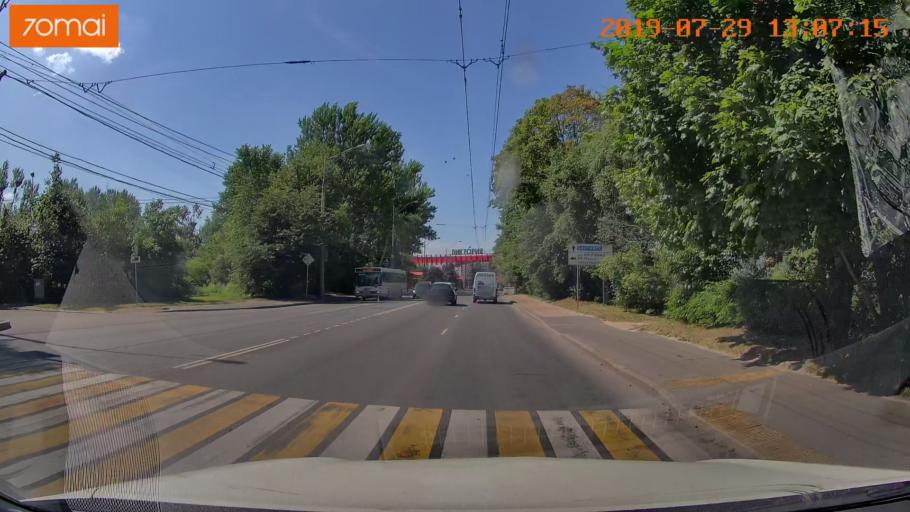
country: RU
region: Kaliningrad
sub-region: Gorod Kaliningrad
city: Kaliningrad
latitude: 54.7108
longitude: 20.4470
